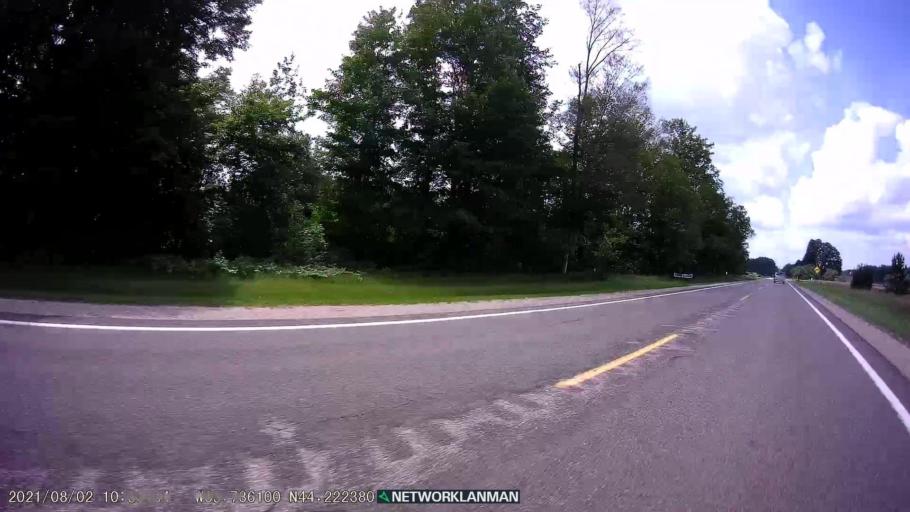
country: US
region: Michigan
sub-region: Lake County
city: Baldwin
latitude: 44.2224
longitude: -85.7866
